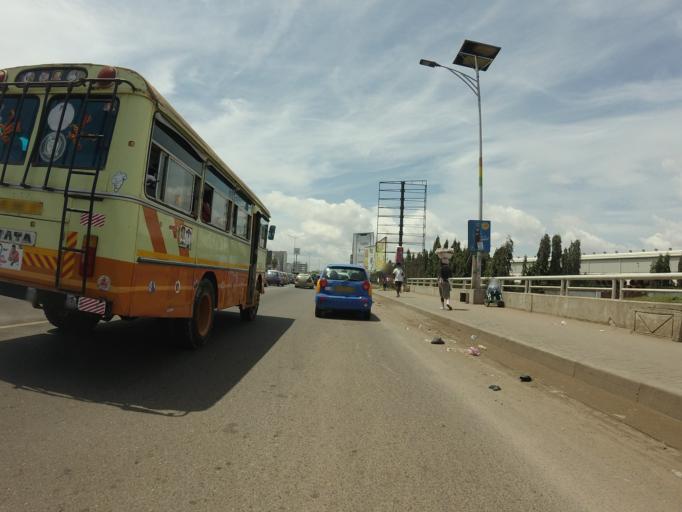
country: GH
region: Greater Accra
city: Accra
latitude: 5.5566
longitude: -0.2212
